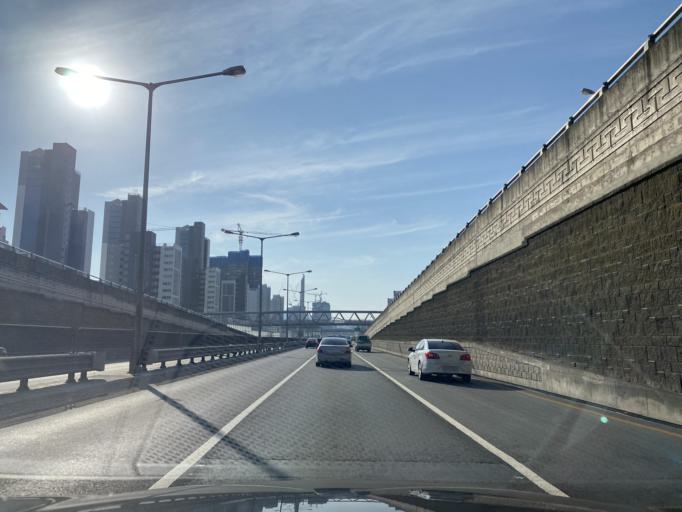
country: KR
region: Chungcheongnam-do
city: Cheonan
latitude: 36.7815
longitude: 127.0917
